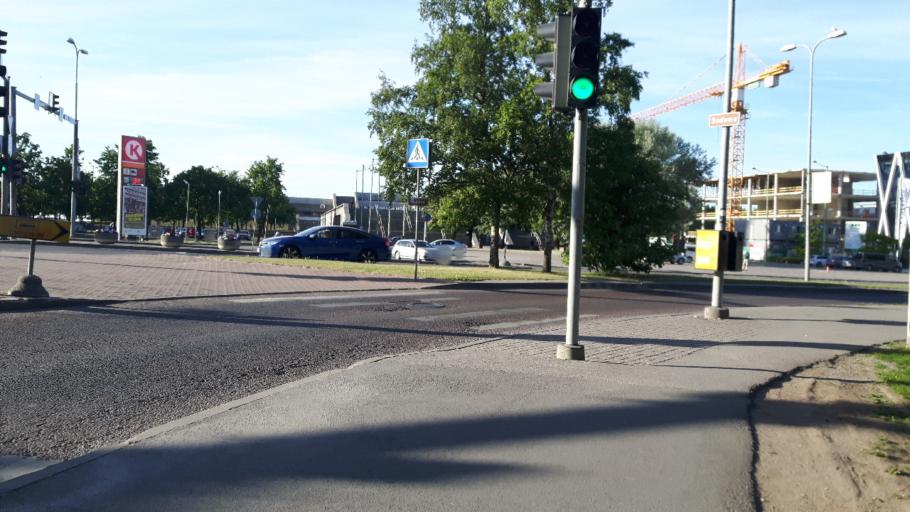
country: EE
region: Harju
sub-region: Tallinna linn
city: Tallinn
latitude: 59.4432
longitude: 24.7534
